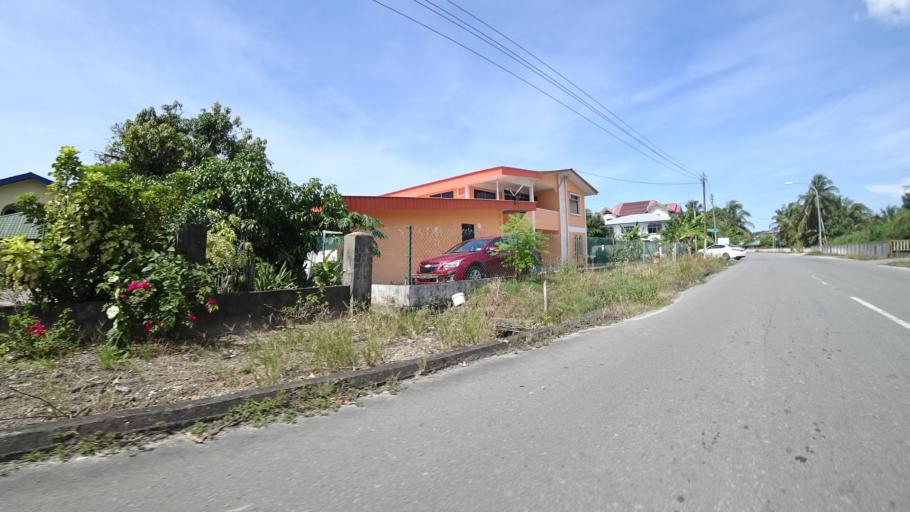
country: BN
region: Brunei and Muara
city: Bandar Seri Begawan
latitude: 4.8906
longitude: 114.8484
